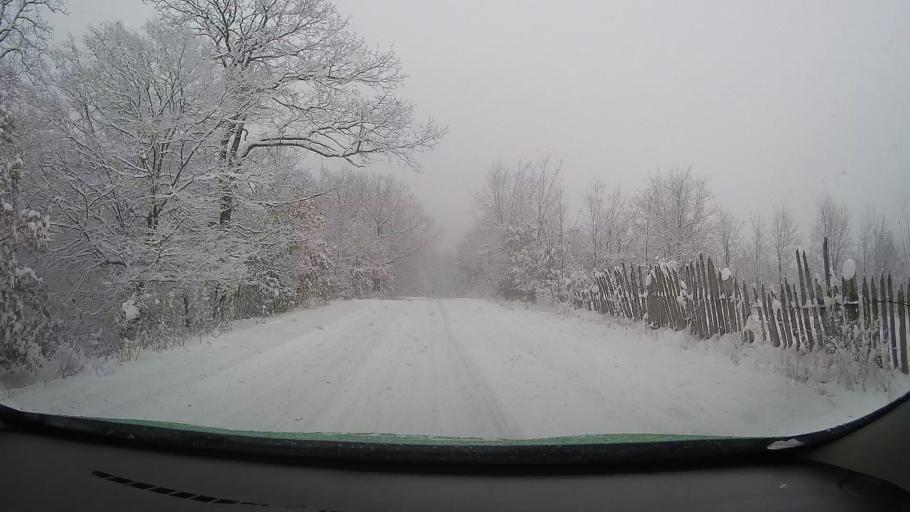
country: RO
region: Hunedoara
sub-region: Comuna Teliucu Inferior
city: Teliucu Inferior
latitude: 45.6902
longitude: 22.8944
